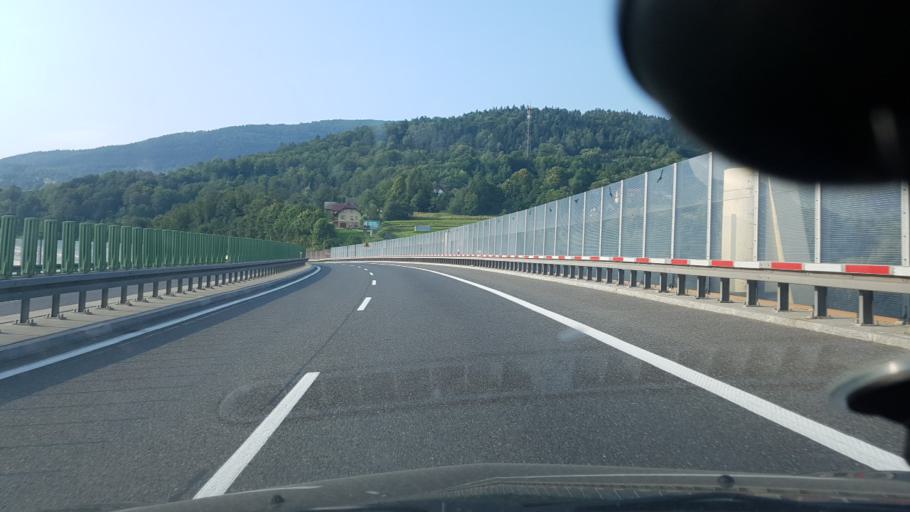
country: PL
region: Lesser Poland Voivodeship
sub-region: Powiat myslenicki
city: Stroza
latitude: 49.7960
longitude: 19.9235
